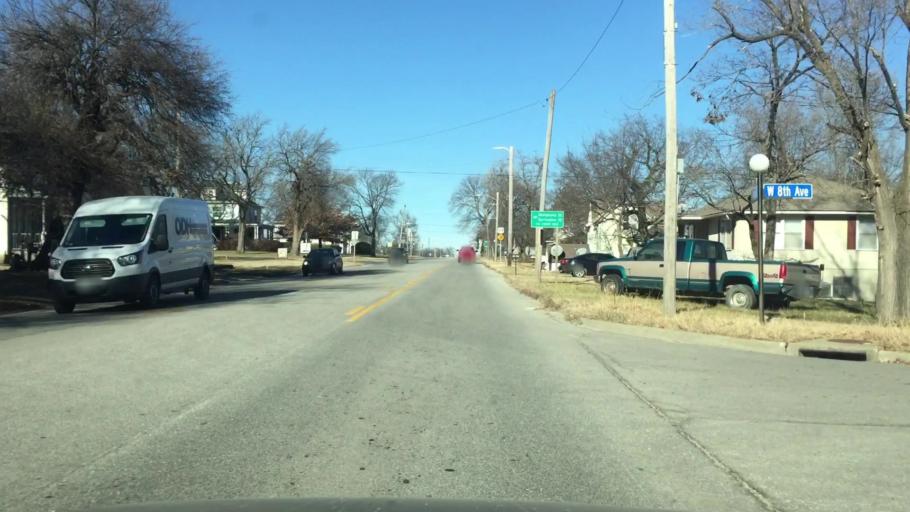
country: US
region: Kansas
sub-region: Anderson County
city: Garnett
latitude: 38.2769
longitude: -95.2493
